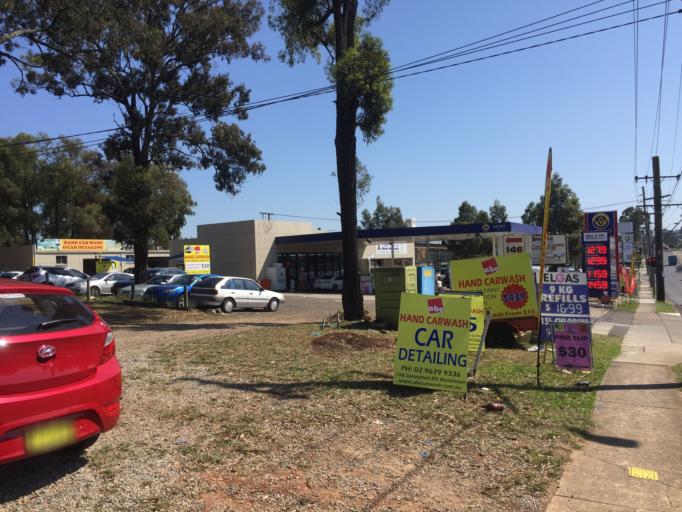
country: AU
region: New South Wales
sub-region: Blacktown
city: Blacktown
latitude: -33.7534
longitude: 150.9151
